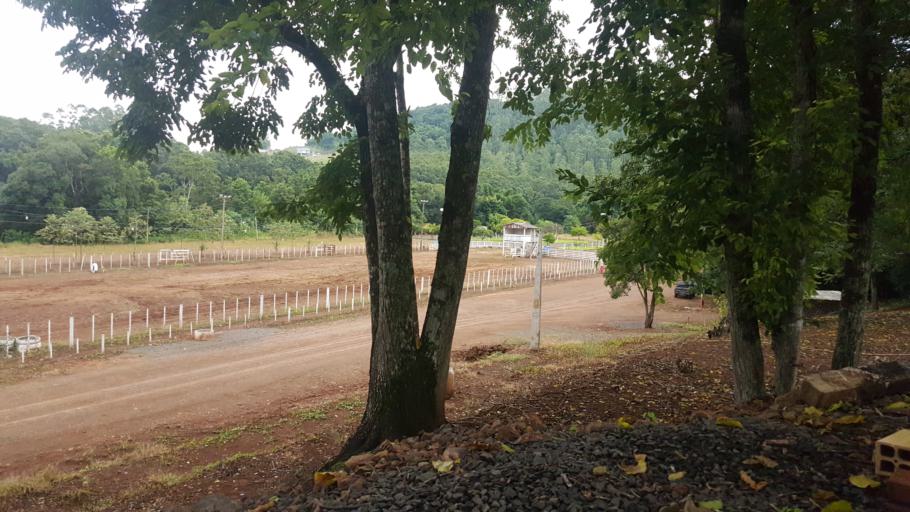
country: BR
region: Rio Grande do Sul
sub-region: Frederico Westphalen
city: Frederico Westphalen
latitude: -27.0896
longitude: -53.3818
